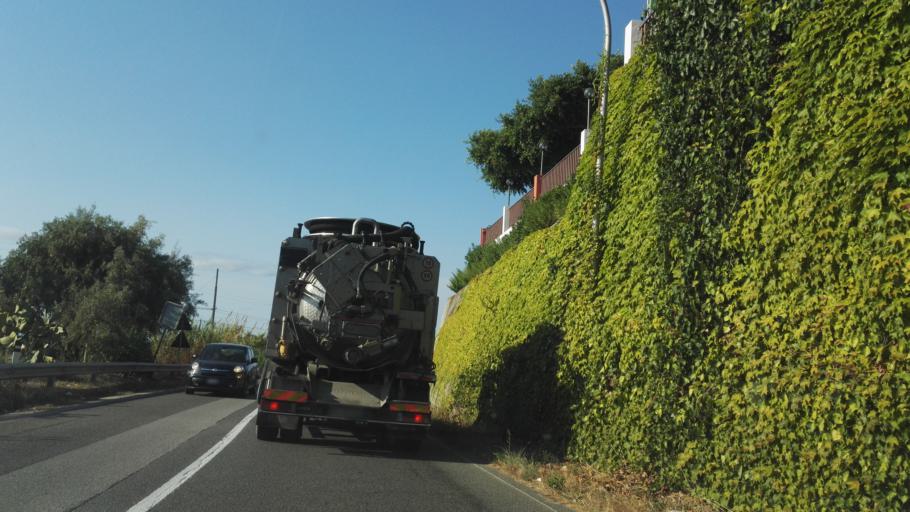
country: IT
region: Calabria
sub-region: Provincia di Vibo-Valentia
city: Zambrone
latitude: 38.7081
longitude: 15.9755
